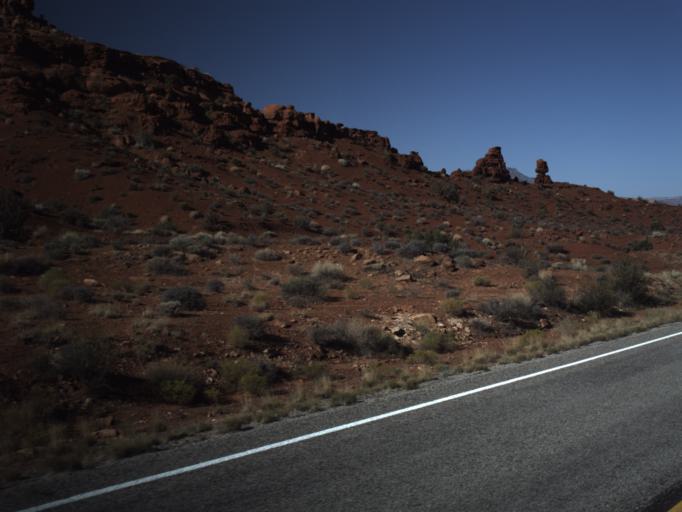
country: US
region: Utah
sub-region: San Juan County
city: Blanding
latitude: 37.8095
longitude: -110.3295
